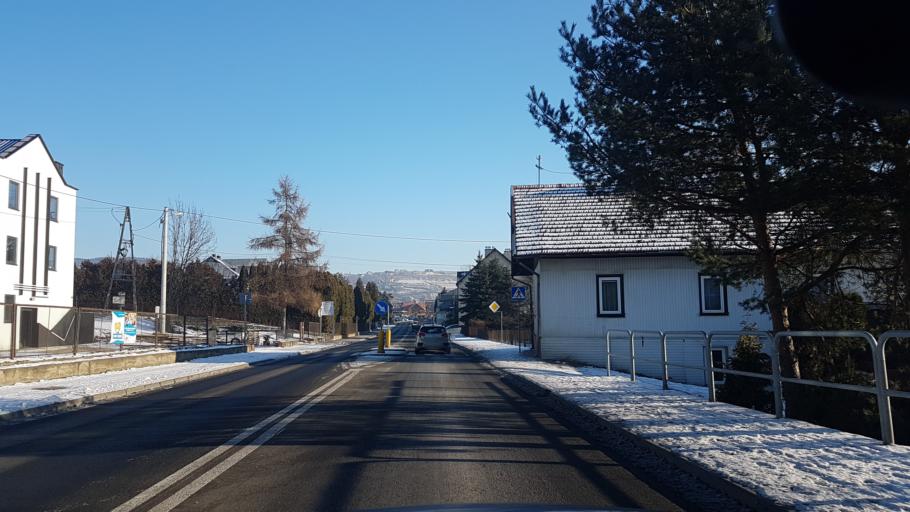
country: PL
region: Lesser Poland Voivodeship
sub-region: Powiat nowosadecki
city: Lacko
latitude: 49.5557
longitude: 20.4319
